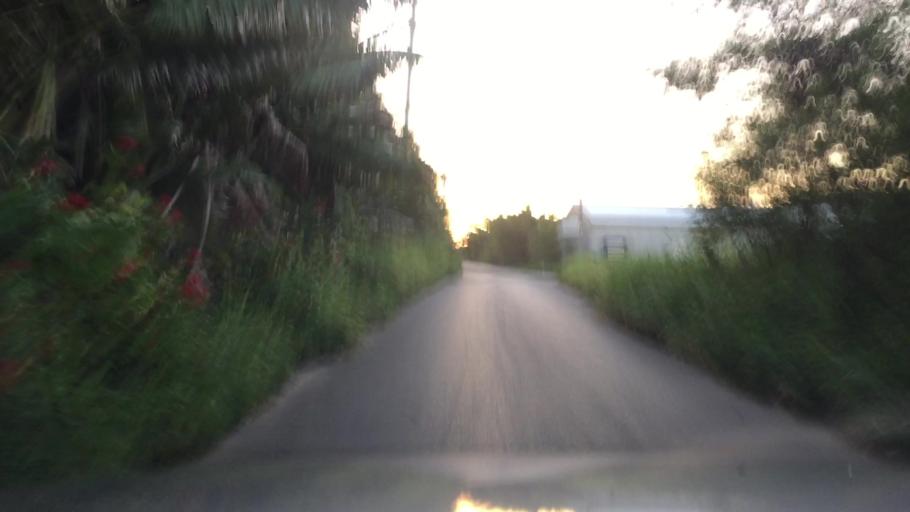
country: JP
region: Okinawa
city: Ishigaki
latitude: 24.3549
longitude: 124.1615
